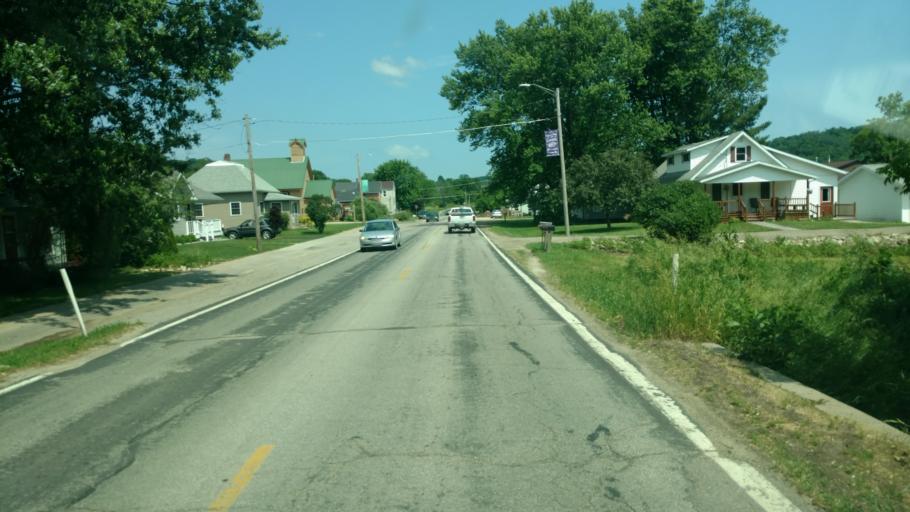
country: US
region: Wisconsin
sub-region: Monroe County
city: Cashton
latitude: 43.5743
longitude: -90.6338
